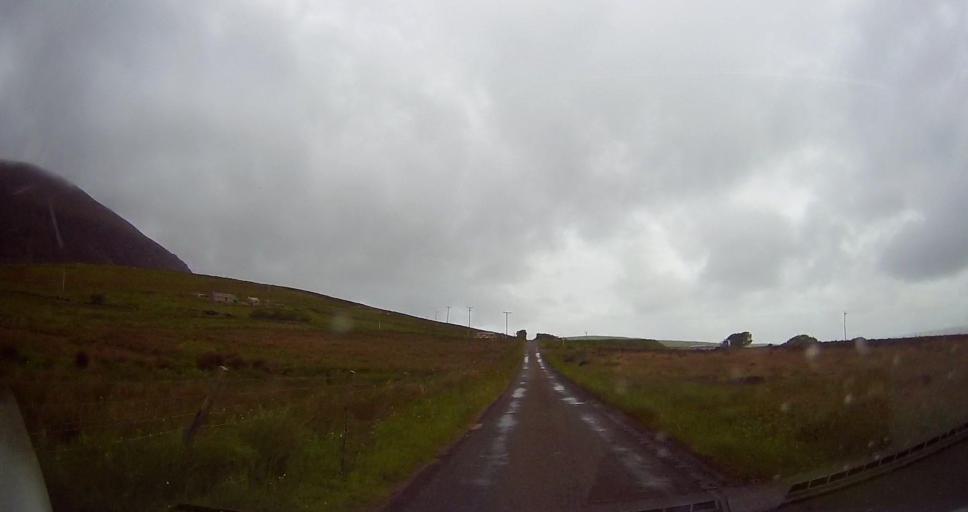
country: GB
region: Scotland
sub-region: Orkney Islands
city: Stromness
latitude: 58.9046
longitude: -3.3135
